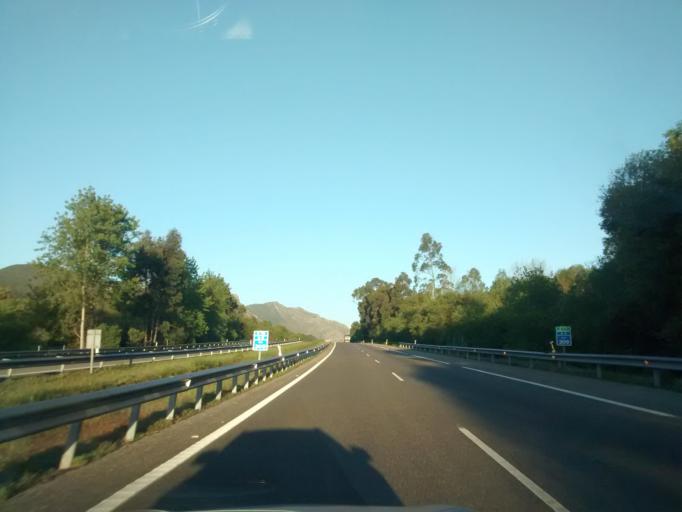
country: ES
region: Asturias
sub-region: Province of Asturias
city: Ribadesella
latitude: 43.4453
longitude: -4.9241
